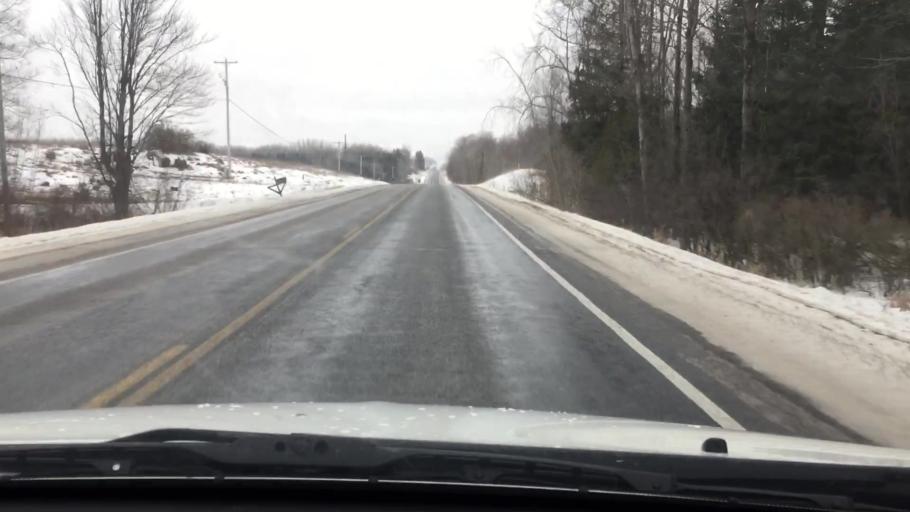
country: US
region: Michigan
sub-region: Osceola County
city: Reed City
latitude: 44.0530
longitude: -85.4439
